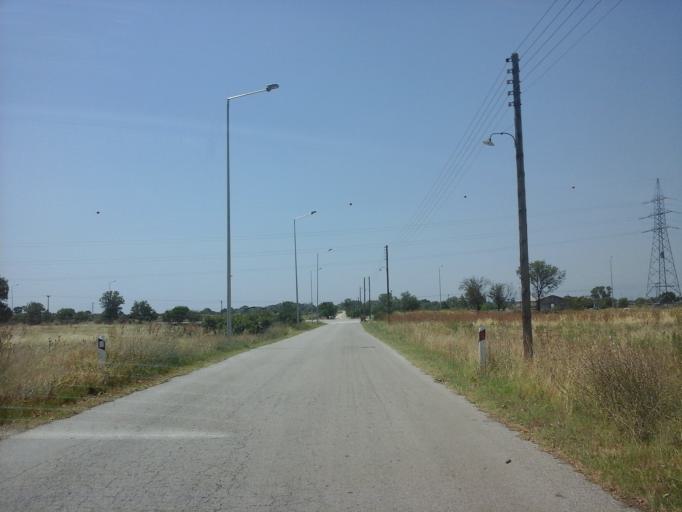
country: GR
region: East Macedonia and Thrace
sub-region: Nomos Evrou
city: Feres
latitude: 40.8632
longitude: 26.0339
